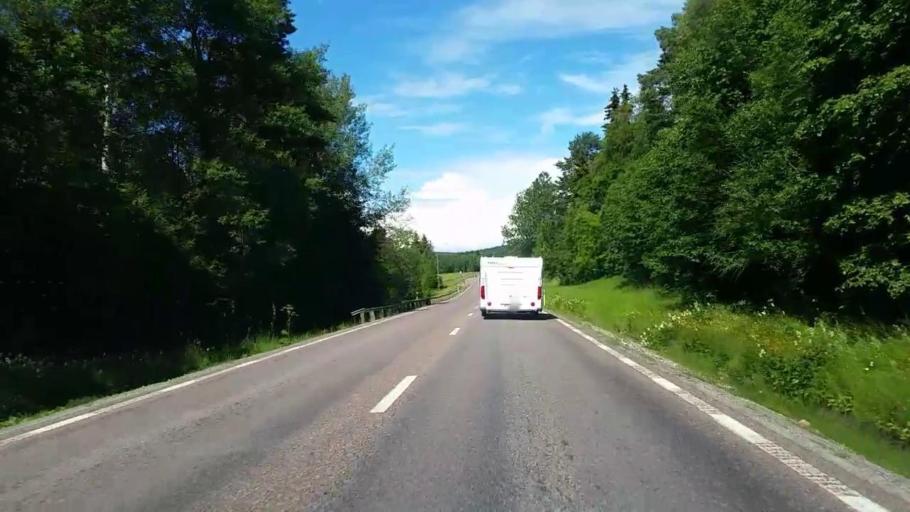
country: SE
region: Dalarna
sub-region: Rattviks Kommun
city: Raettvik
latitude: 60.9877
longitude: 15.2203
